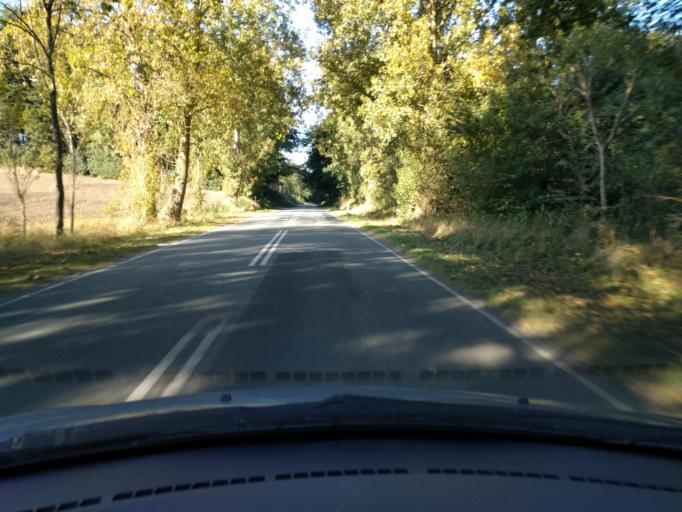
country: DK
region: South Denmark
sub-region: Assens Kommune
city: Assens
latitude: 55.2139
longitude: 9.9974
